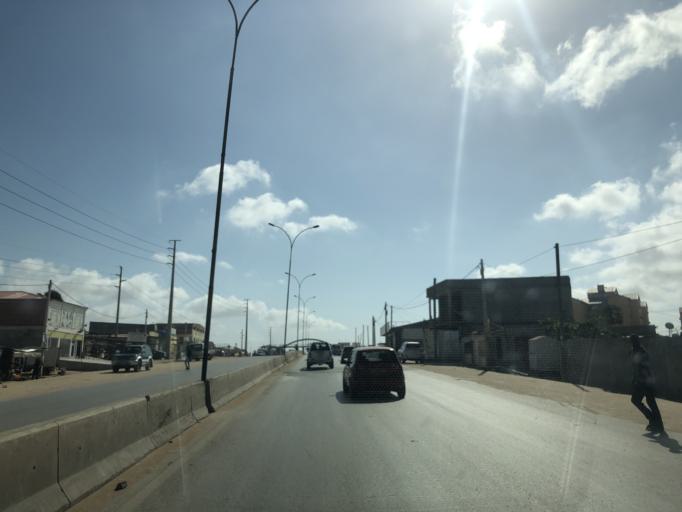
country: AO
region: Luanda
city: Luanda
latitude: -8.9074
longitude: 13.2424
